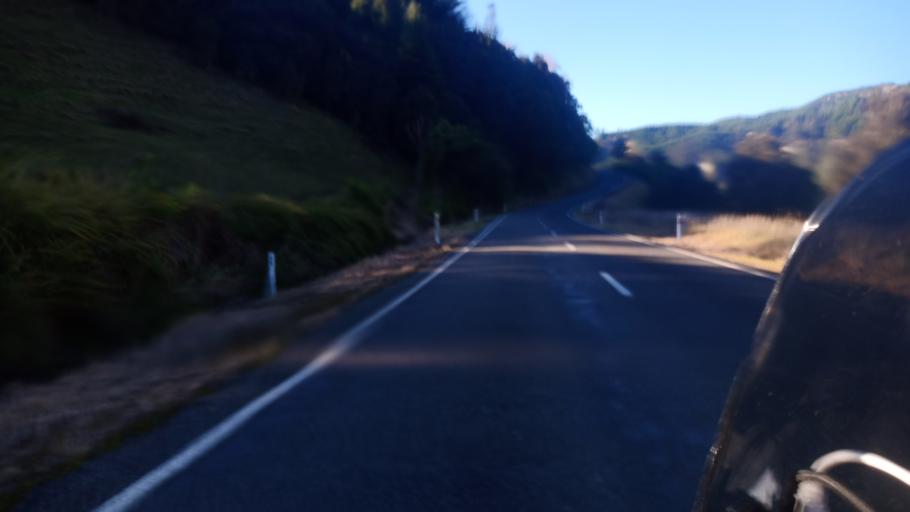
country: NZ
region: Hawke's Bay
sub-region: Wairoa District
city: Wairoa
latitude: -38.8764
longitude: 177.2228
